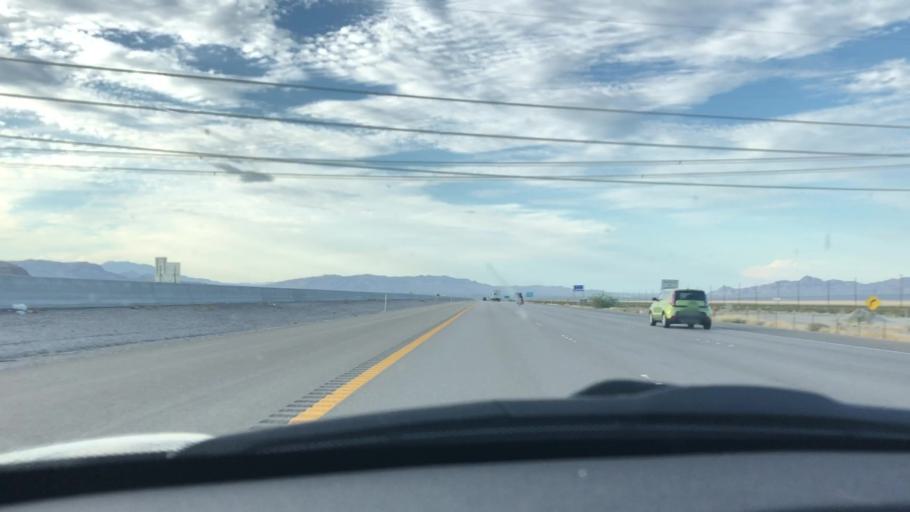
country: US
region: Nevada
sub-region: Clark County
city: Sandy Valley
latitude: 35.6229
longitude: -115.3864
